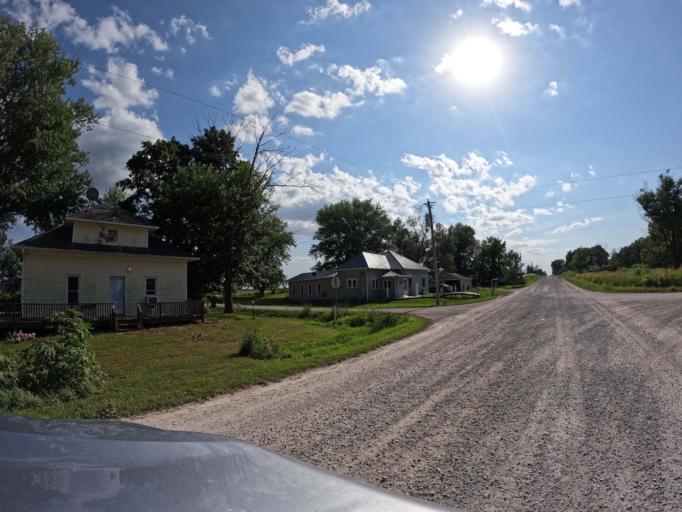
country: US
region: Iowa
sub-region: Appanoose County
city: Centerville
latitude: 40.7179
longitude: -93.0301
